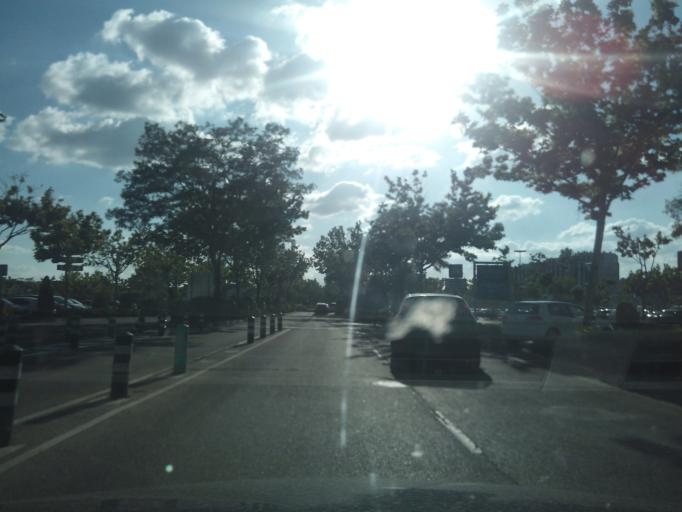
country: ES
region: Madrid
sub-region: Provincia de Madrid
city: San Sebastian de los Reyes
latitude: 40.5442
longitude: -3.6104
